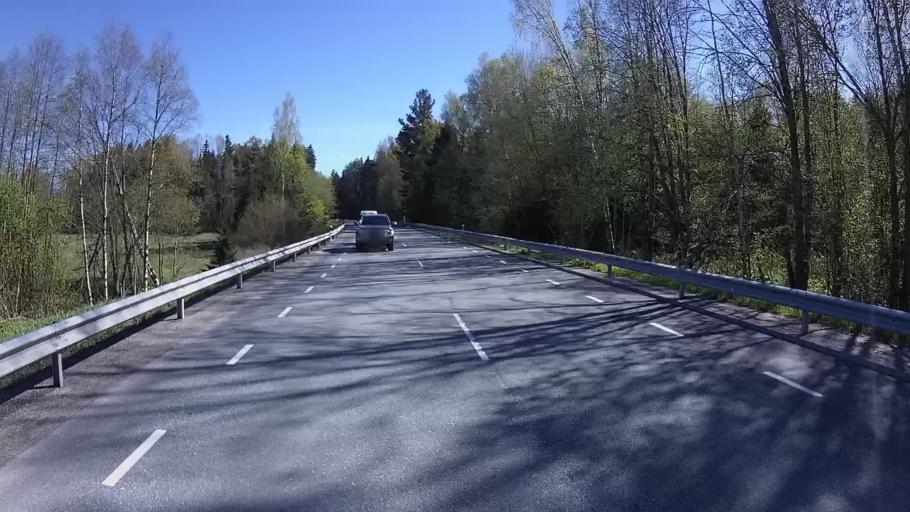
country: EE
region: Harju
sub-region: Loksa linn
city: Loksa
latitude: 59.5590
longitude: 25.7245
